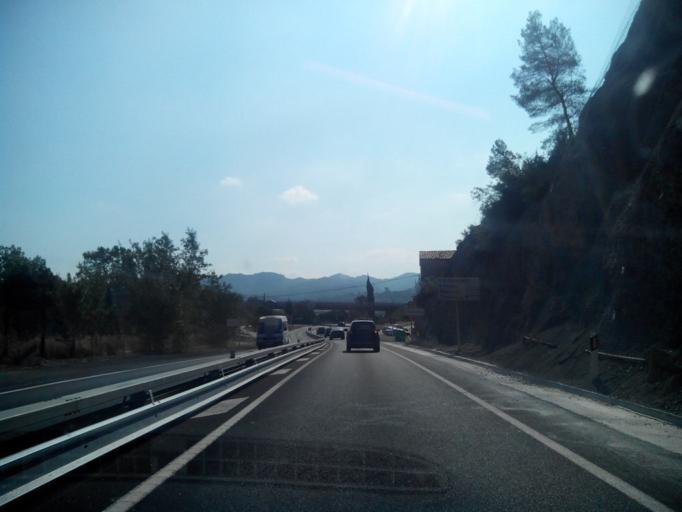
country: ES
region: Catalonia
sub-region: Provincia de Barcelona
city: Manresa
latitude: 41.6787
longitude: 1.8435
